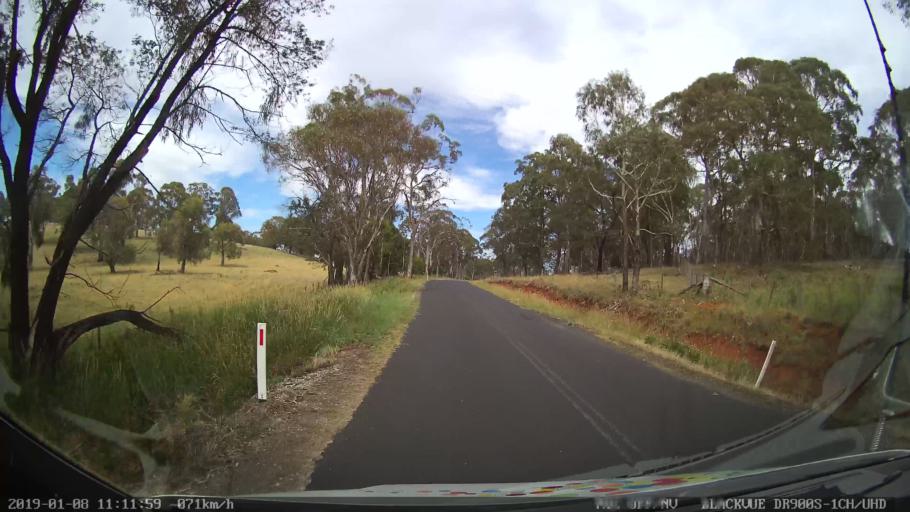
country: AU
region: New South Wales
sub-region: Guyra
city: Guyra
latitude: -30.2270
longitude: 151.6173
